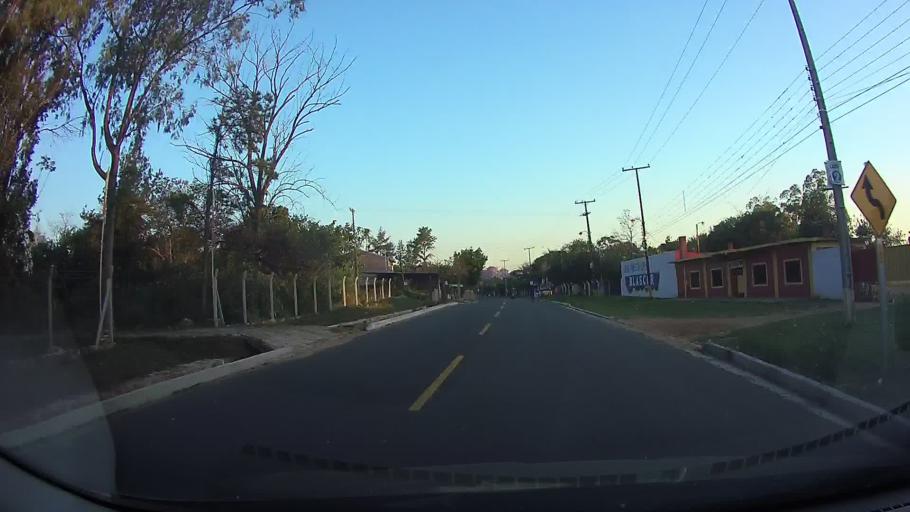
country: PY
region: Central
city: Limpio
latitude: -25.2378
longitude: -57.4909
